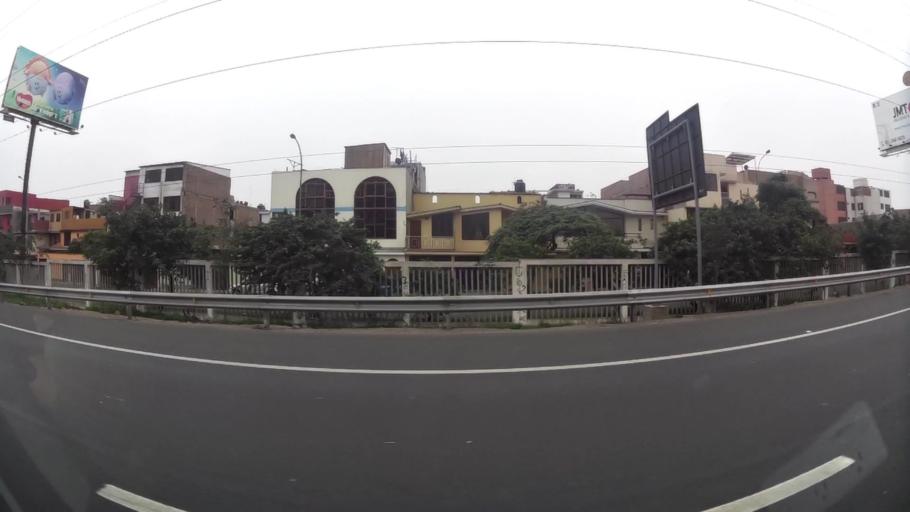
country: PE
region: Lima
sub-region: Lima
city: Surco
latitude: -12.1397
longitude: -76.9811
